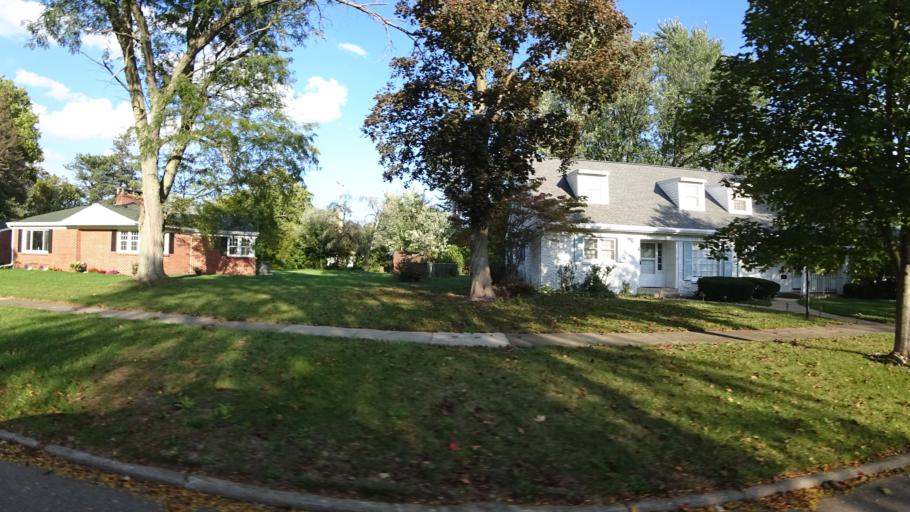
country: US
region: Michigan
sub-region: Saint Joseph County
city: Three Rivers
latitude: 41.9568
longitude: -85.6321
